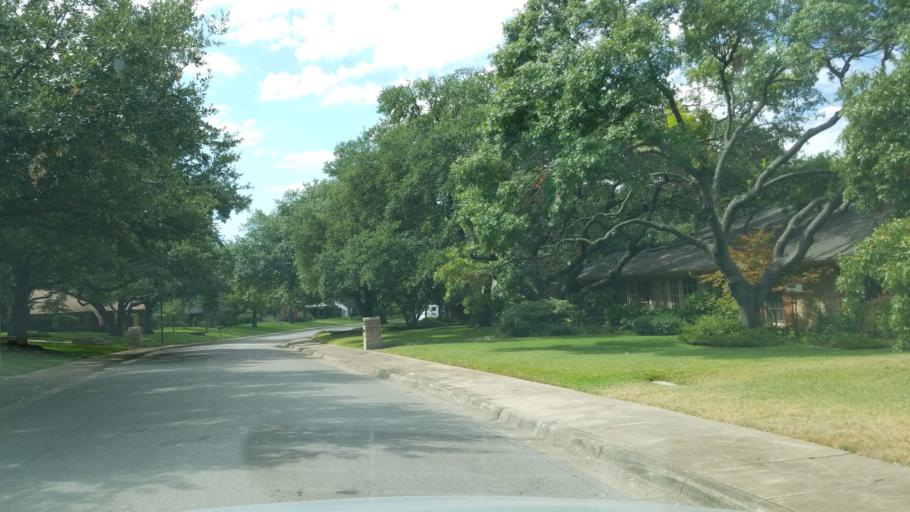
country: US
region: Texas
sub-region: Dallas County
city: Addison
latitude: 32.9582
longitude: -96.7886
